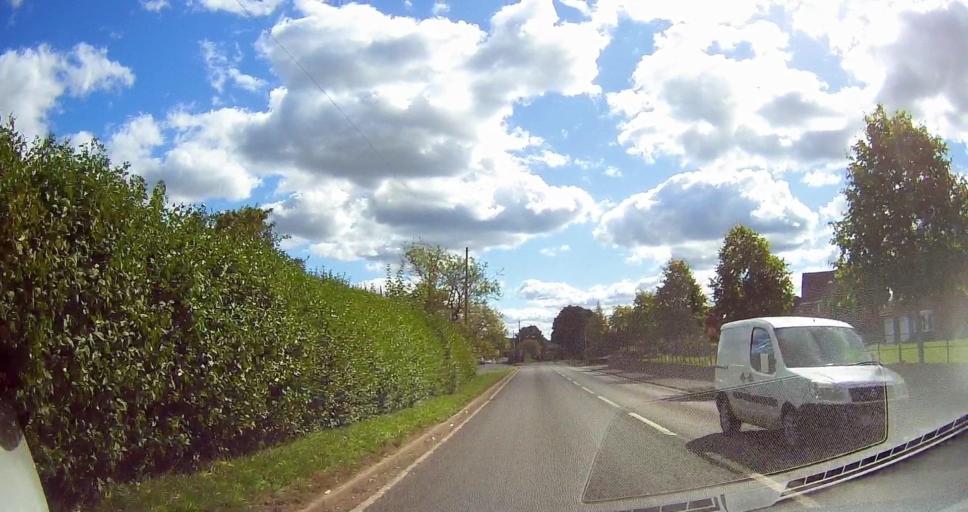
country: GB
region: England
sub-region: Cheshire East
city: Chorlton
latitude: 52.9647
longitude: -2.3930
